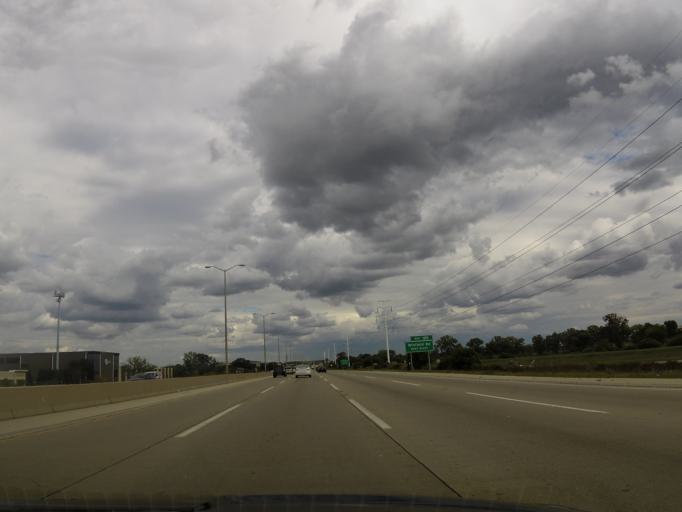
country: US
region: Illinois
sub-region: DuPage County
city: Warrenville
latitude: 41.8052
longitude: -88.1839
